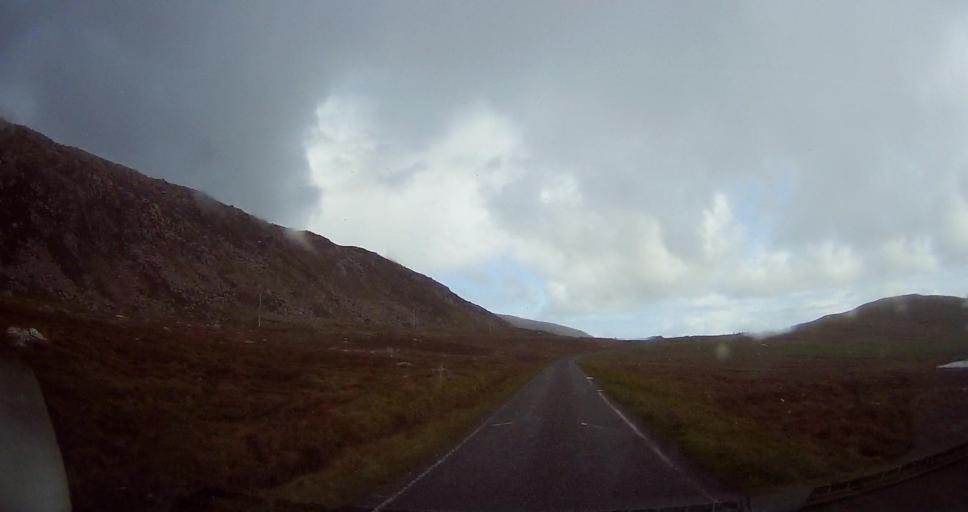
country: GB
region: Scotland
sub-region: Shetland Islands
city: Lerwick
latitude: 60.5503
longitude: -1.3405
